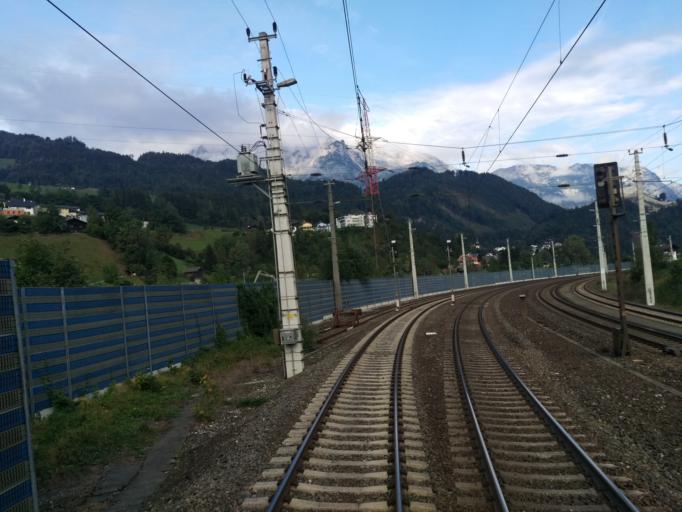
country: AT
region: Salzburg
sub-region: Politischer Bezirk Sankt Johann im Pongau
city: Werfen
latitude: 47.4693
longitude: 13.1965
